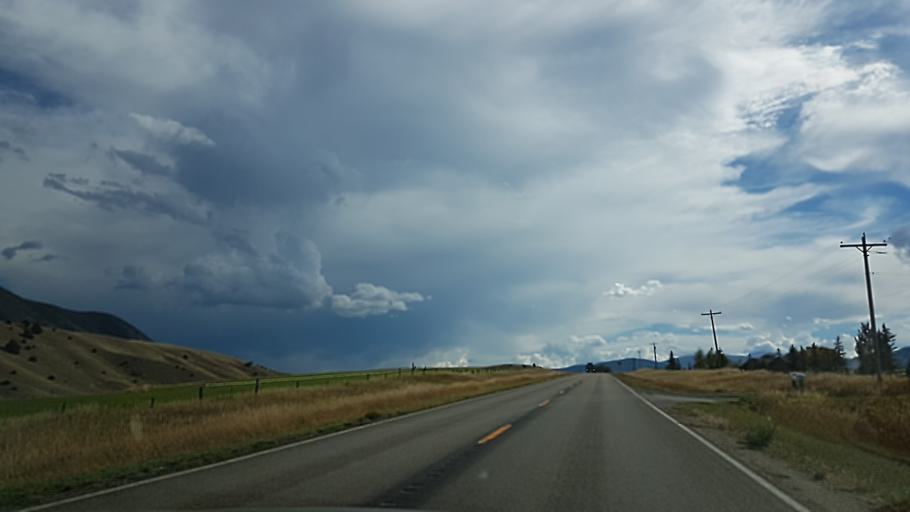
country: US
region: Montana
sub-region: Jefferson County
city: Whitehall
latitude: 45.8426
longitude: -111.9404
